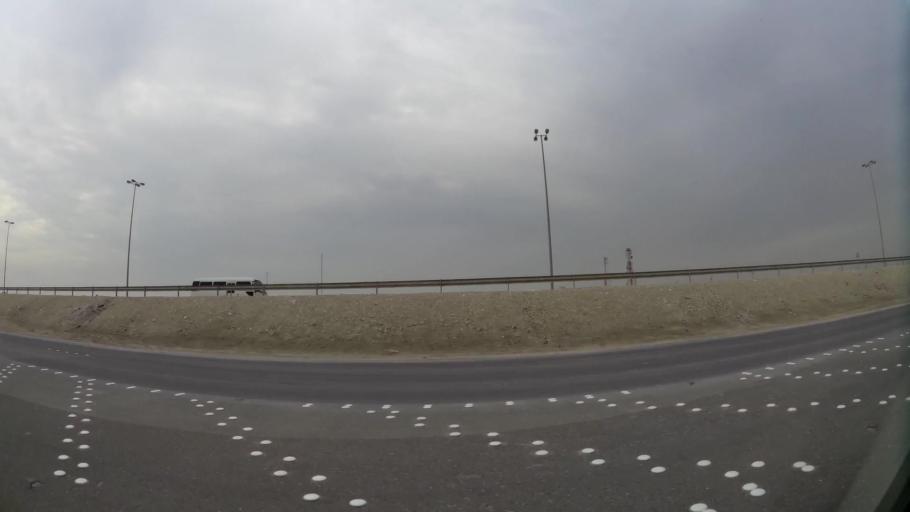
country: BH
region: Northern
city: Sitrah
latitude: 26.0716
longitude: 50.6156
